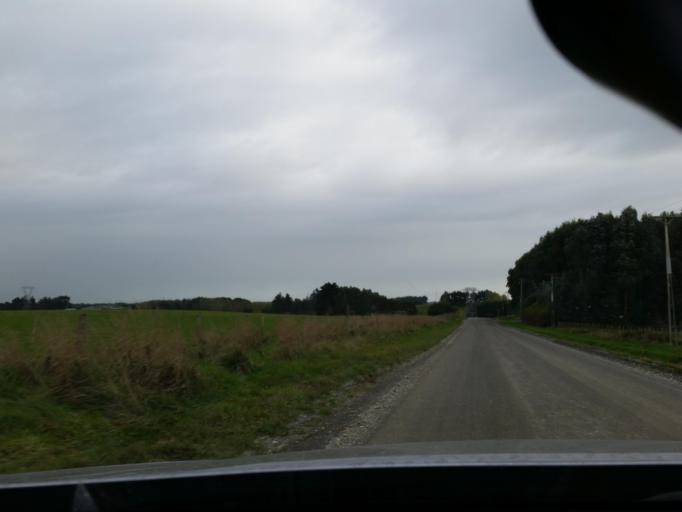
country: NZ
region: Southland
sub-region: Invercargill City
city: Invercargill
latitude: -46.3572
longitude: 168.4222
